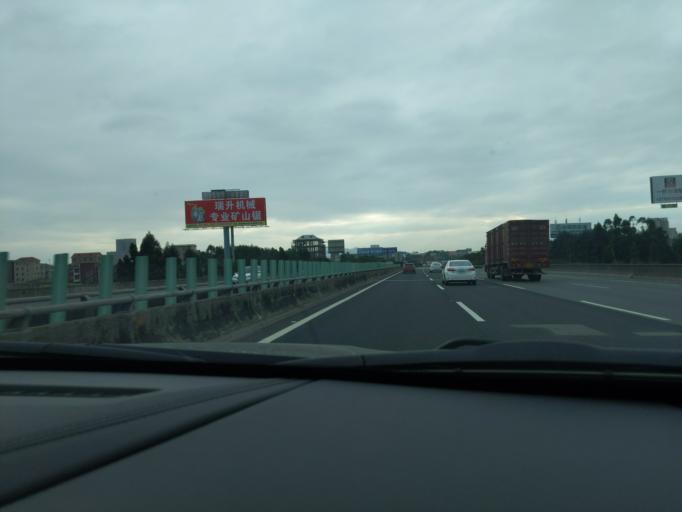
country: CN
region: Fujian
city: Anhai
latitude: 24.7378
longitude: 118.4228
